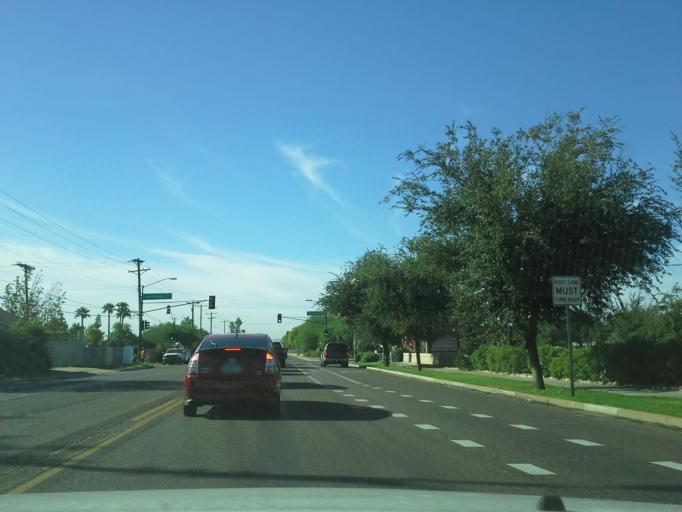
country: US
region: Arizona
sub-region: Maricopa County
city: Phoenix
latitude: 33.5211
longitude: -112.0912
